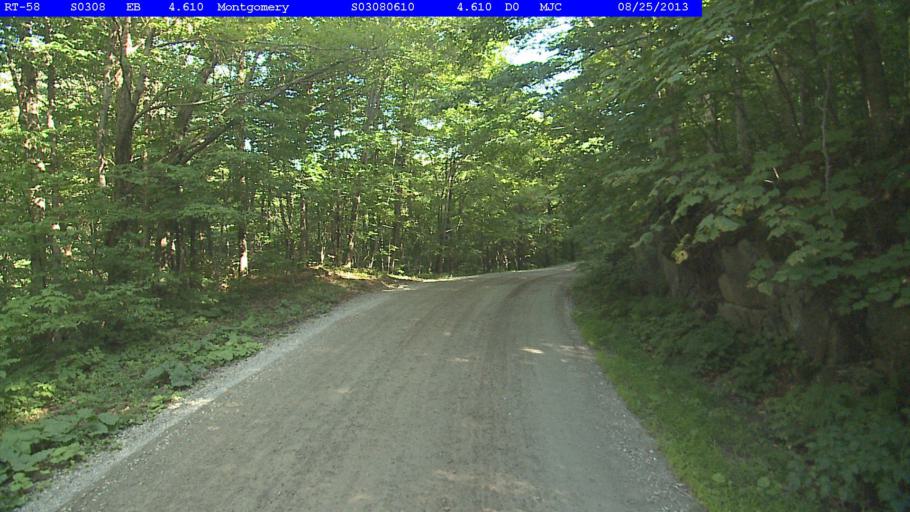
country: US
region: Vermont
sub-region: Franklin County
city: Richford
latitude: 44.8432
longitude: -72.5358
